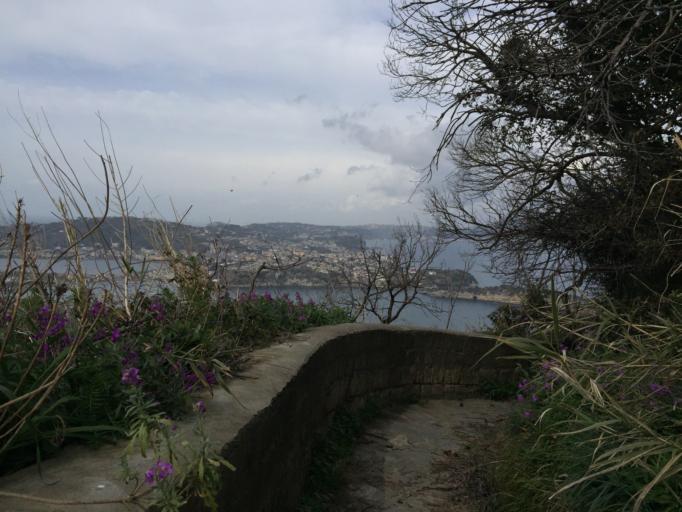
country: IT
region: Campania
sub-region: Provincia di Napoli
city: Bacoli
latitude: 40.7819
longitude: 14.0864
